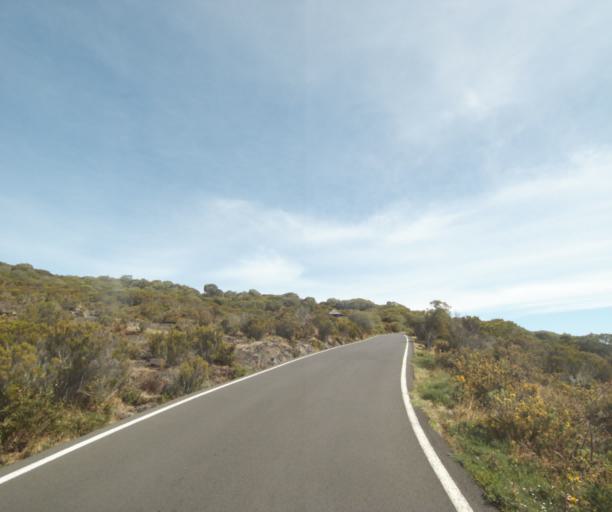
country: RE
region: Reunion
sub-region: Reunion
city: Trois-Bassins
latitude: -21.0700
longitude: 55.3793
